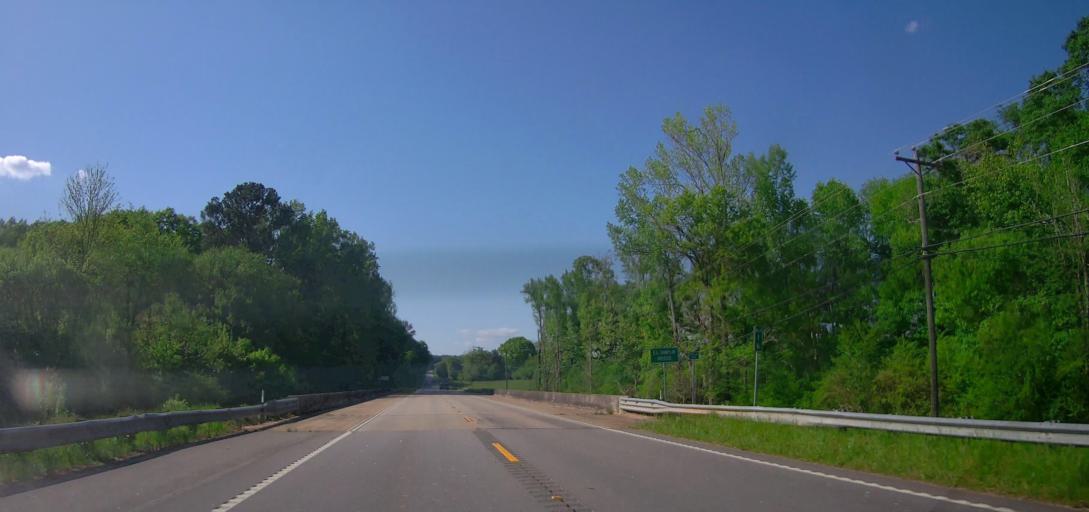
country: US
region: Georgia
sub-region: Morgan County
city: Madison
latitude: 33.6369
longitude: -83.4899
